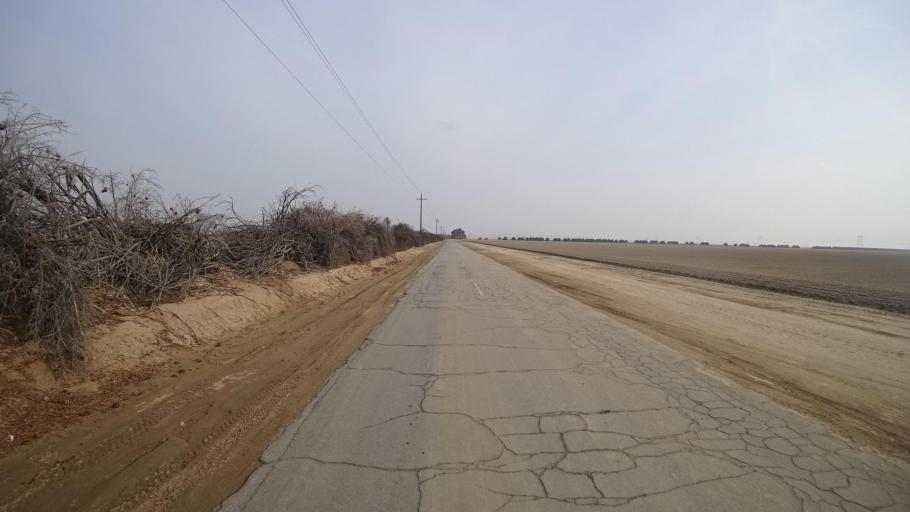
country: US
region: California
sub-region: Kern County
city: Weedpatch
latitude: 35.1365
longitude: -118.9222
